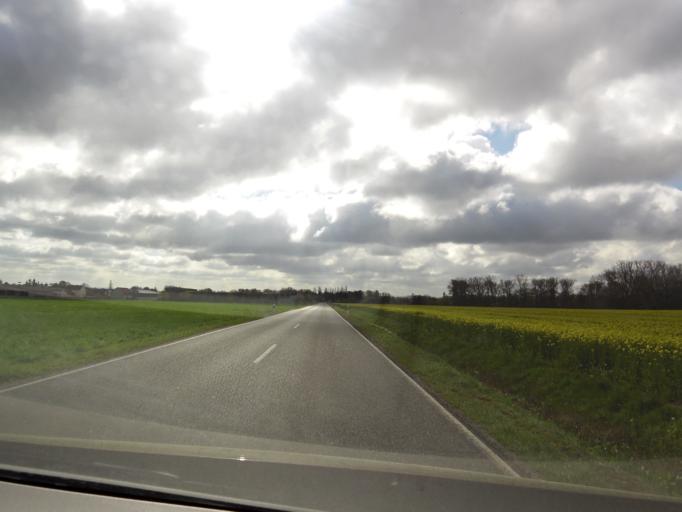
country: DE
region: Thuringia
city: Wandersleben
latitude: 50.9047
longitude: 10.8410
